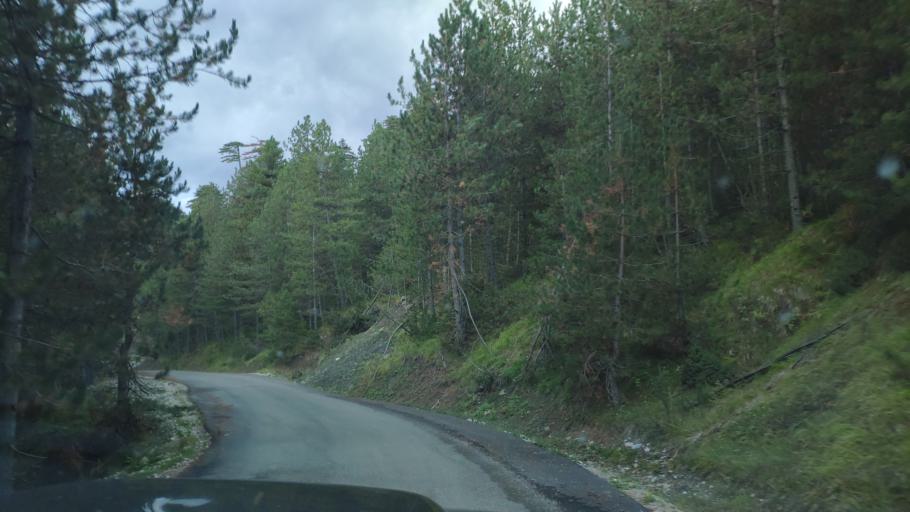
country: AL
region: Korce
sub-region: Rrethi i Kolonjes
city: Erseke
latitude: 40.2930
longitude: 20.8645
